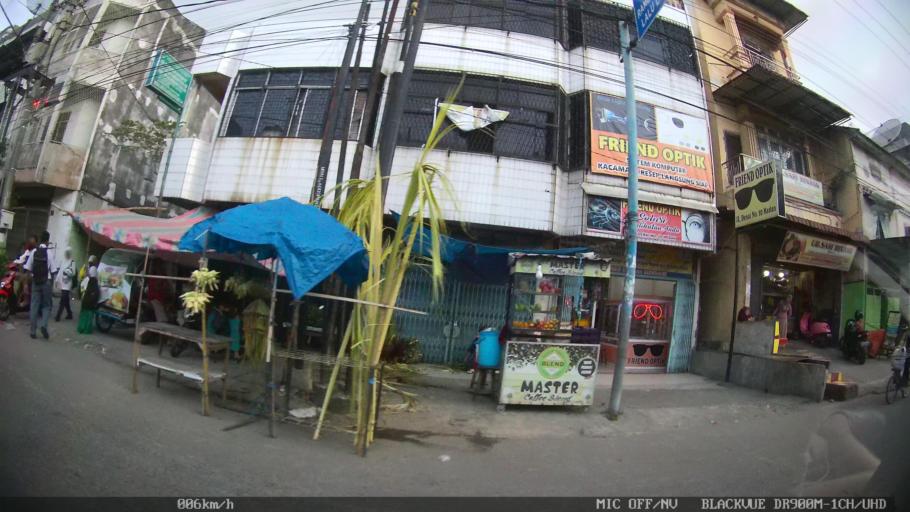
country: ID
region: North Sumatra
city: Medan
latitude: 3.5820
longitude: 98.7052
